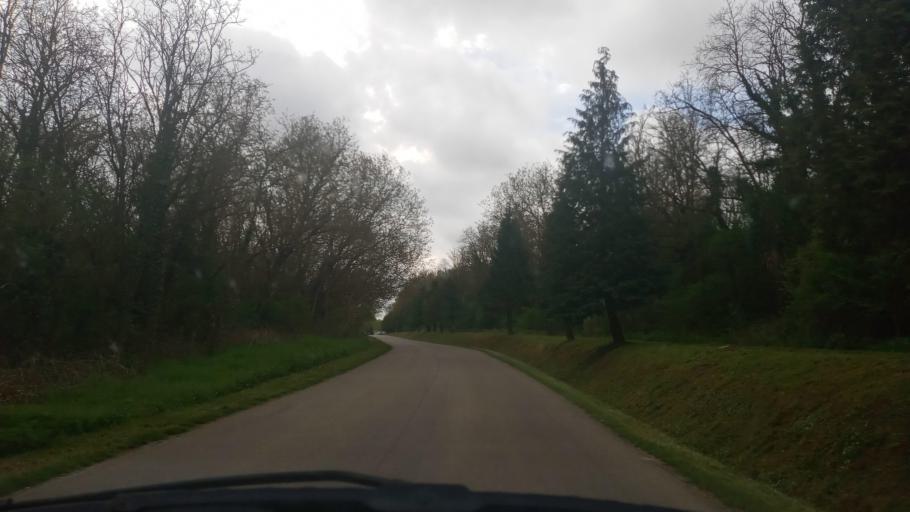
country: HU
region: Baranya
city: Boly
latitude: 45.9902
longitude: 18.4186
